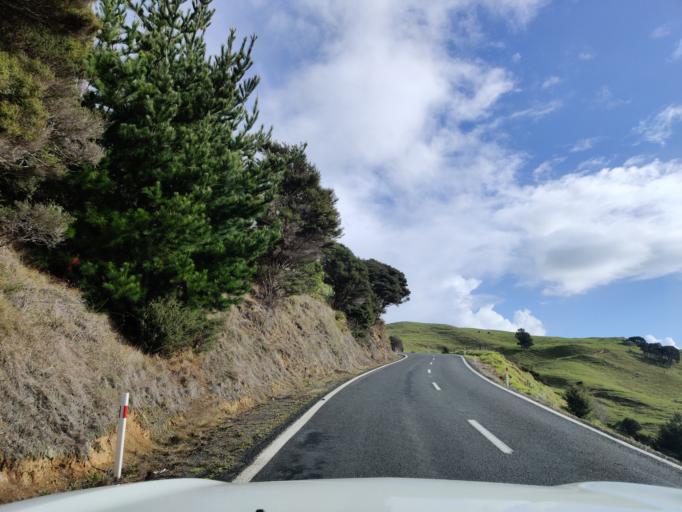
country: NZ
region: Waikato
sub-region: Thames-Coromandel District
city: Coromandel
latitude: -36.8159
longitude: 175.4858
